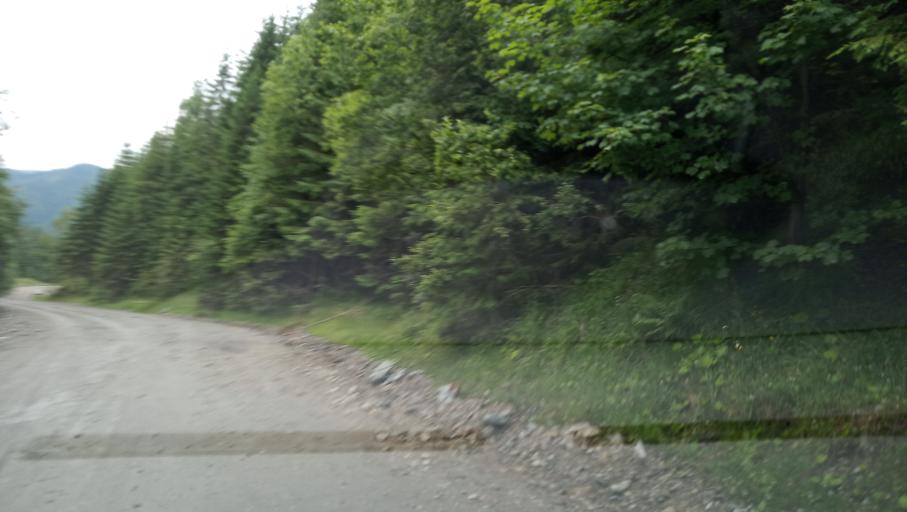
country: RO
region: Hunedoara
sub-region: Oras Petrila
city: Petrila
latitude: 45.4005
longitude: 23.5714
